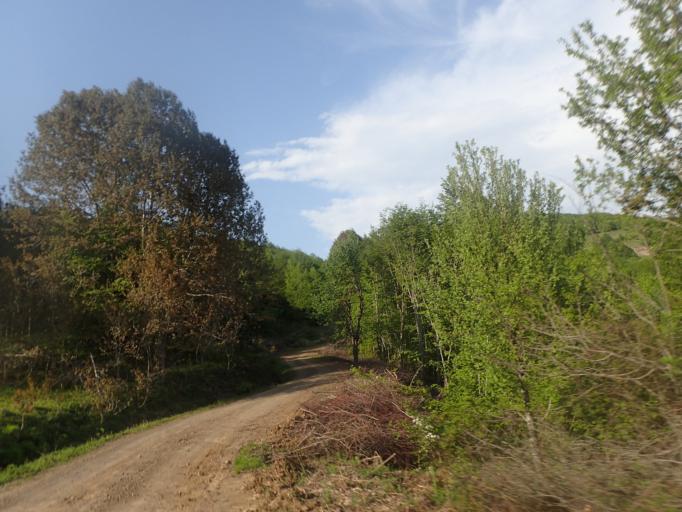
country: TR
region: Ordu
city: Akkus
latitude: 40.8220
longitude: 36.9782
